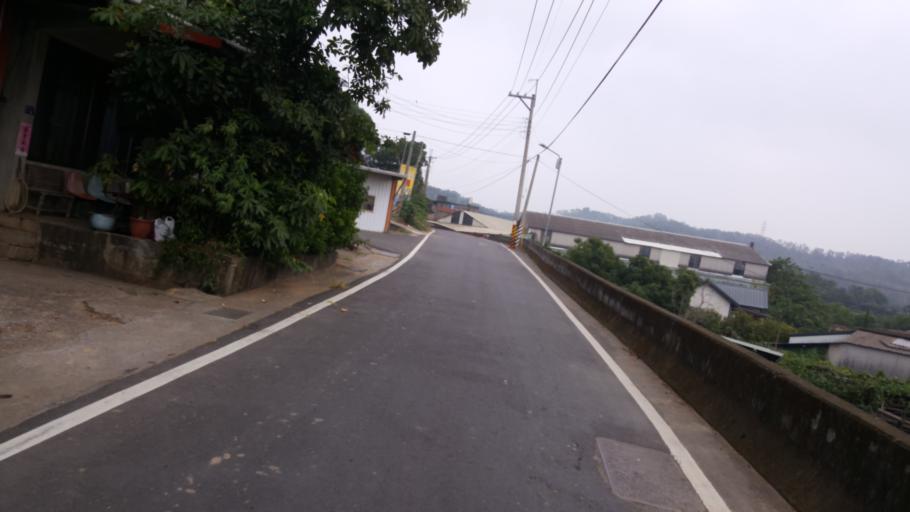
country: TW
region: Taiwan
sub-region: Hsinchu
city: Hsinchu
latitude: 24.7033
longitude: 120.9443
